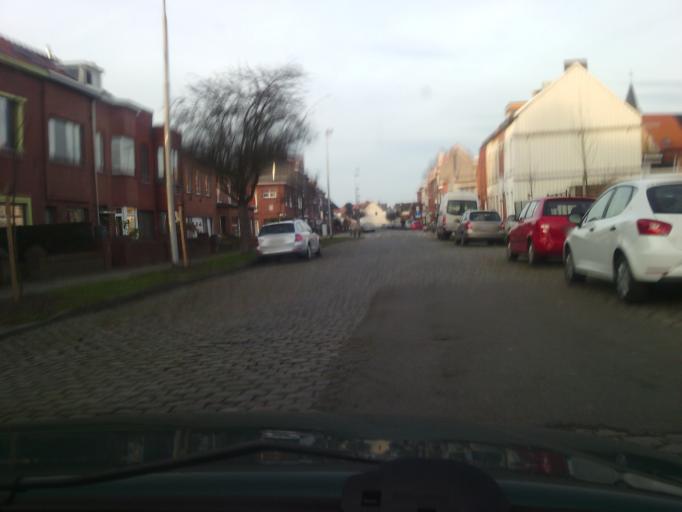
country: BE
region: Flanders
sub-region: Provincie Oost-Vlaanderen
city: Gent
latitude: 51.0615
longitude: 3.6917
